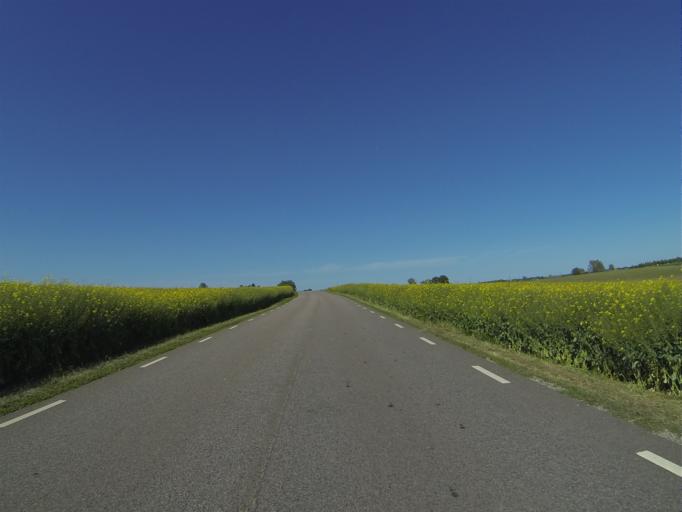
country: SE
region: Skane
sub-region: Staffanstorps Kommun
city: Hjaerup
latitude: 55.6087
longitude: 13.1441
